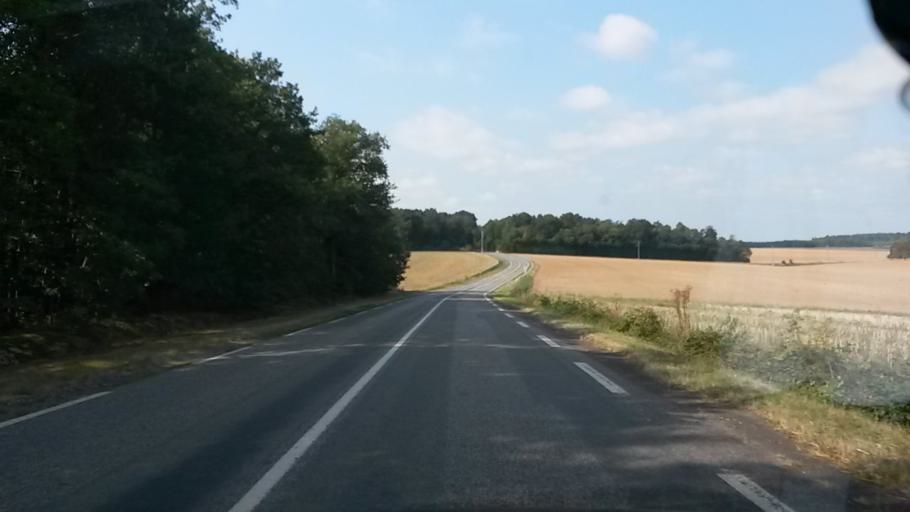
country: FR
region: Haute-Normandie
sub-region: Departement de l'Eure
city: Damville
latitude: 48.8386
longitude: 1.0308
